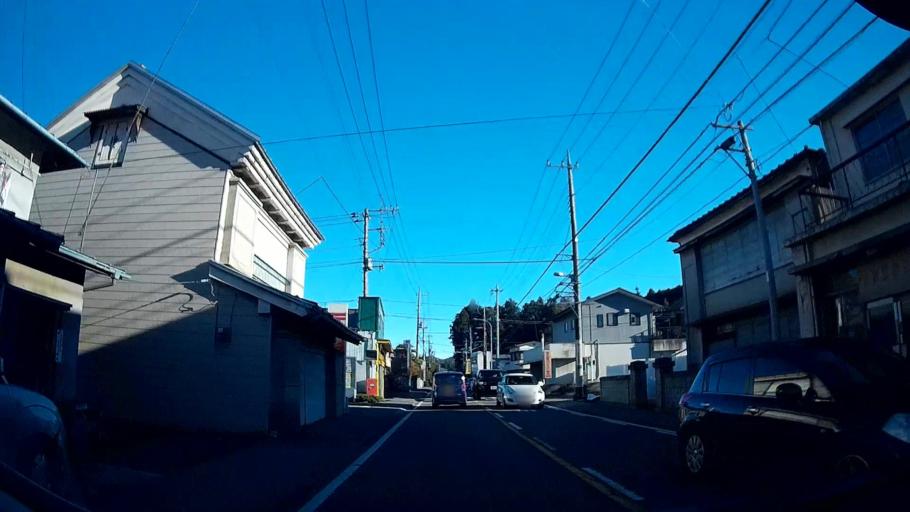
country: JP
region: Yamanashi
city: Fujikawaguchiko
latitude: 35.4744
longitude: 138.7929
